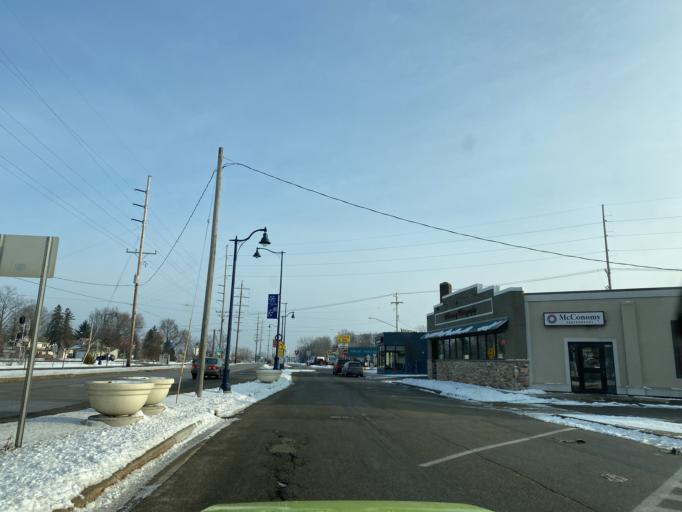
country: US
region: Michigan
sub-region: Ottawa County
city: Hudsonville
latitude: 42.8677
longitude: -85.8662
